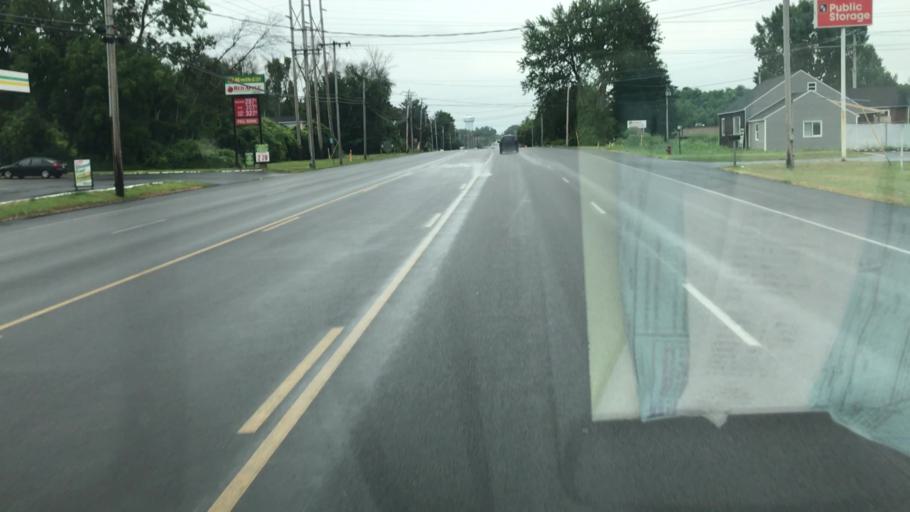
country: US
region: New York
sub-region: Onondaga County
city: Liverpool
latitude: 43.1264
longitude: -76.2180
